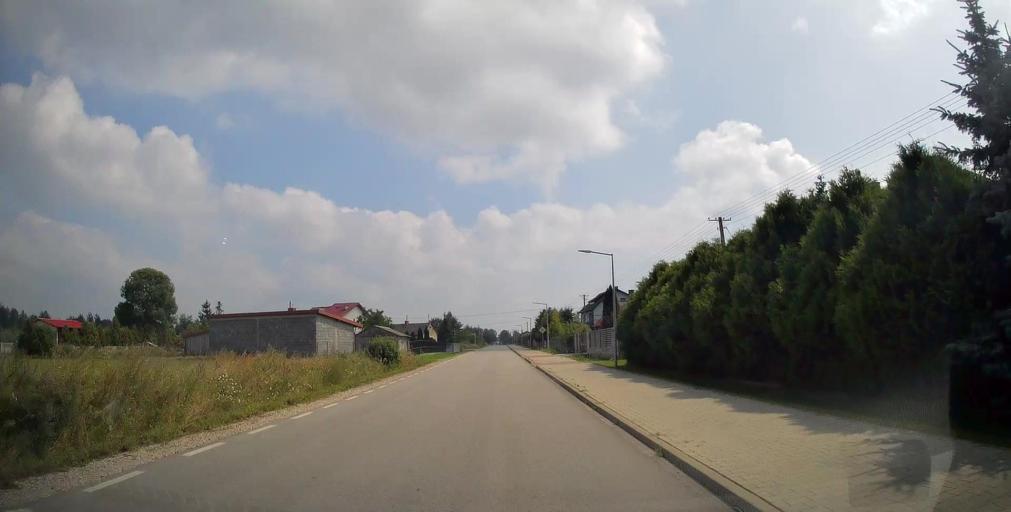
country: PL
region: Masovian Voivodeship
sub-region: Powiat bialobrzeski
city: Sucha
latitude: 51.6114
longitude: 20.9709
